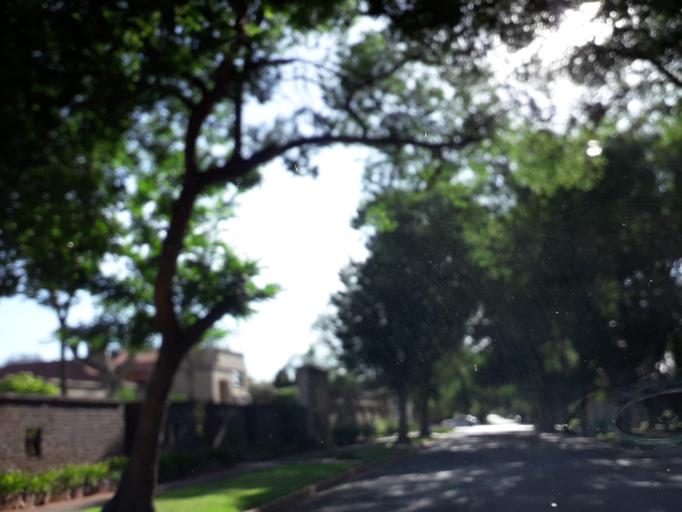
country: ZA
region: Gauteng
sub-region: City of Johannesburg Metropolitan Municipality
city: Johannesburg
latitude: -26.1621
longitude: 28.0110
